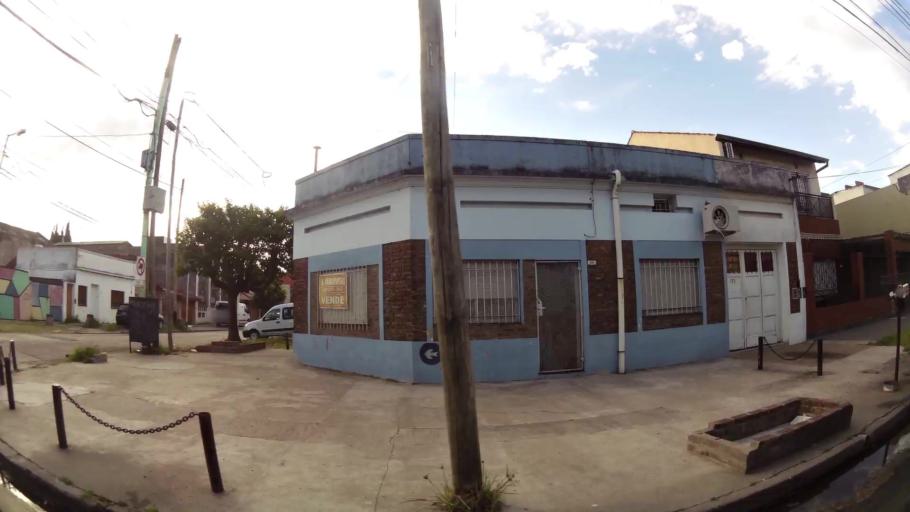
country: AR
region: Buenos Aires
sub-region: Partido de Avellaneda
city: Avellaneda
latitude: -34.6799
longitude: -58.3558
